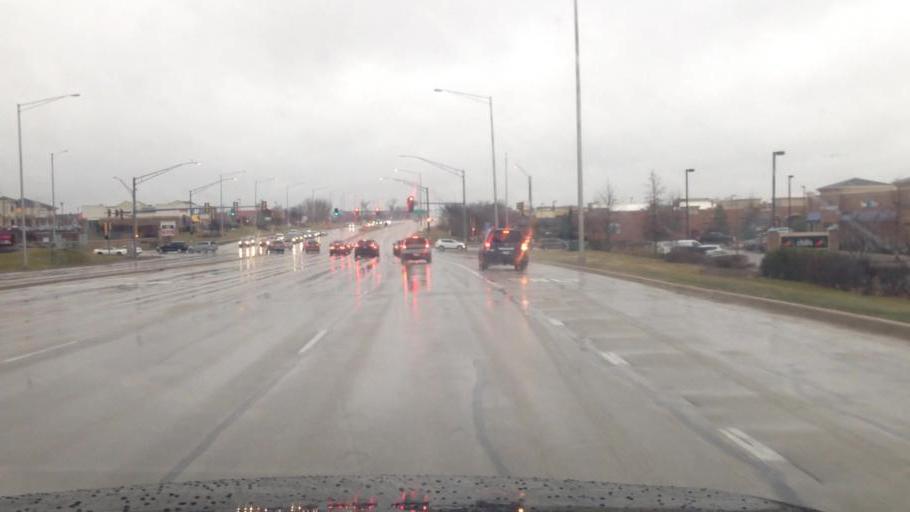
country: US
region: Illinois
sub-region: McHenry County
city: Lake in the Hills
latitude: 42.1553
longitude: -88.3360
